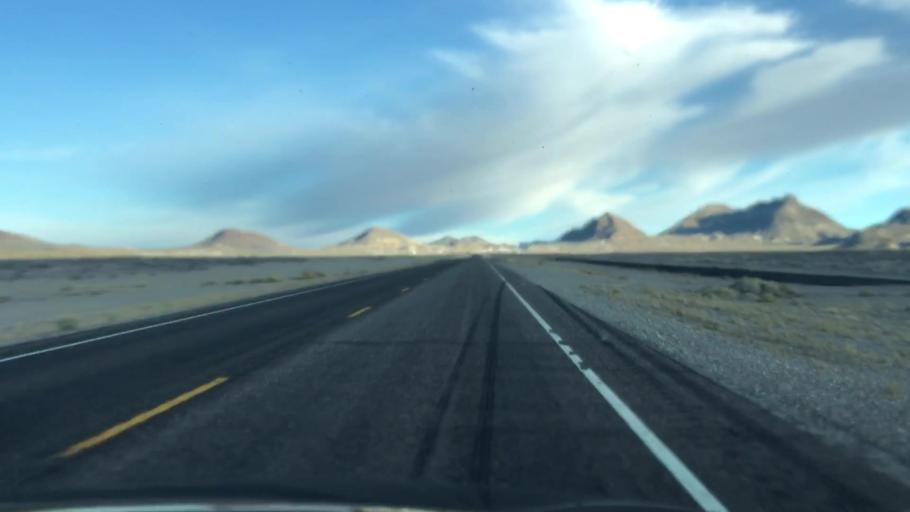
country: US
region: Nevada
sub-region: Nye County
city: Tonopah
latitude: 38.0870
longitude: -117.2876
